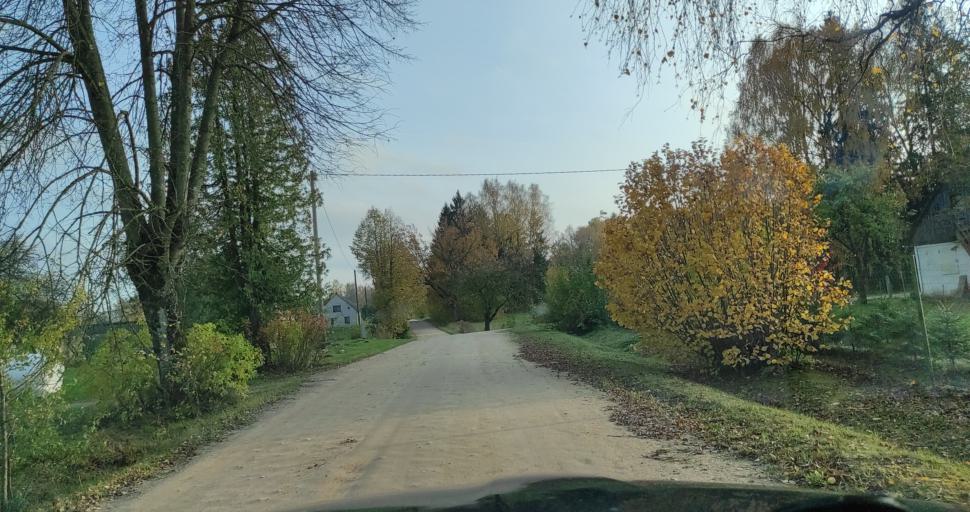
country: LV
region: Vainode
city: Vainode
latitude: 56.4250
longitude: 21.8737
